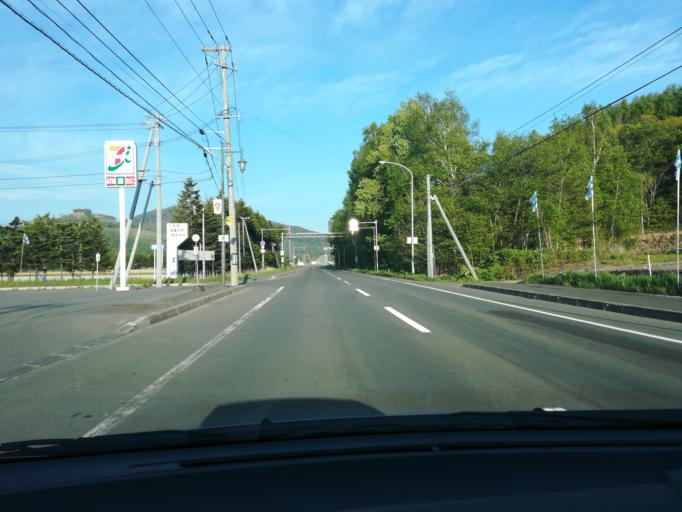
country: JP
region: Hokkaido
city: Shimo-furano
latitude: 43.1617
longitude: 142.5745
